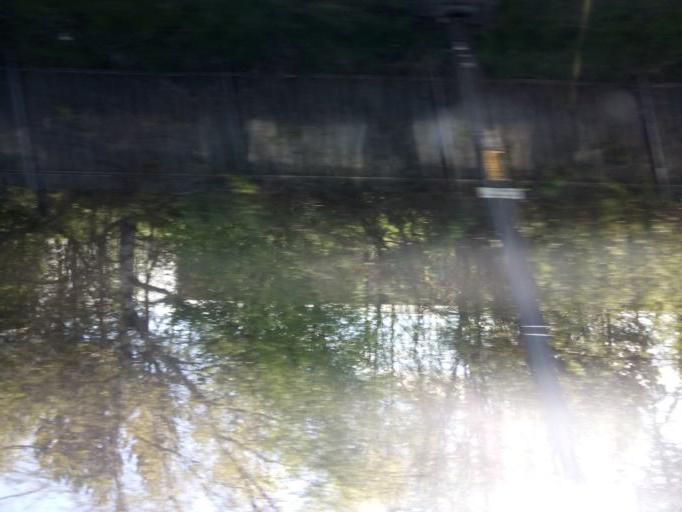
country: GB
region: England
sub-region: Darlington
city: Darlington
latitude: 54.5361
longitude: -1.5426
